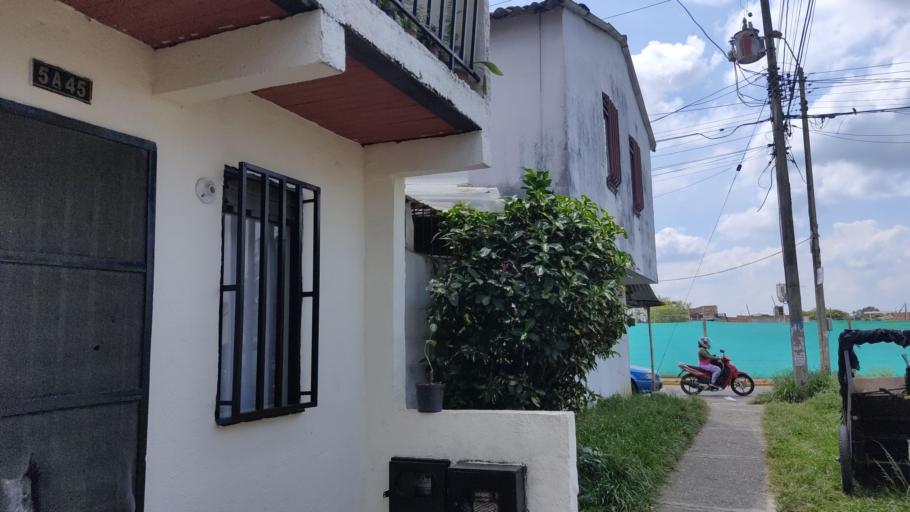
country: CO
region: Valle del Cauca
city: Jamundi
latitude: 3.2513
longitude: -76.5413
